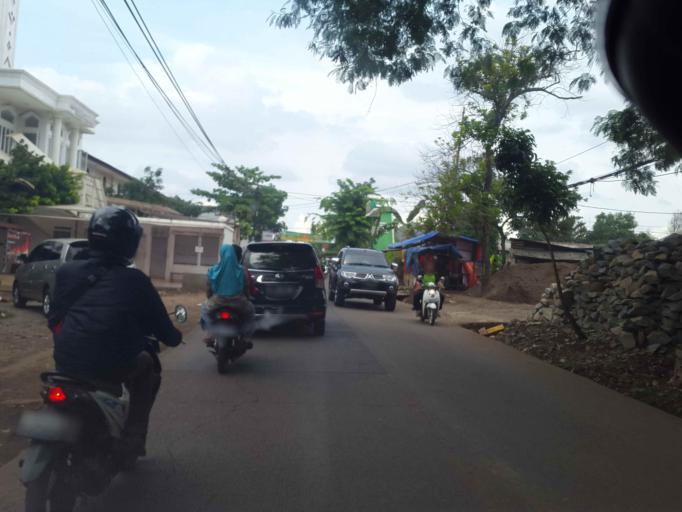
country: ID
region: West Java
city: Cileungsir
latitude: -6.3571
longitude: 106.9205
